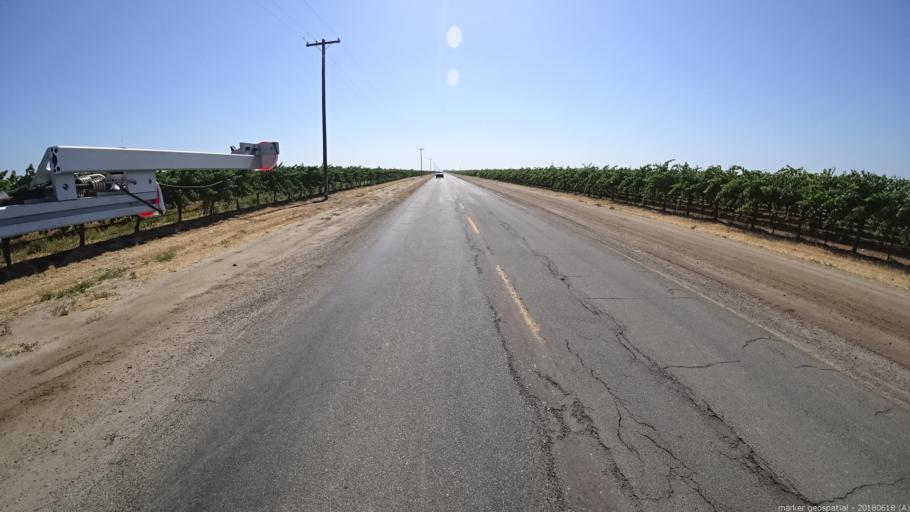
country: US
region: California
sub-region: Fresno County
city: Kerman
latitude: 36.8366
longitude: -120.2097
